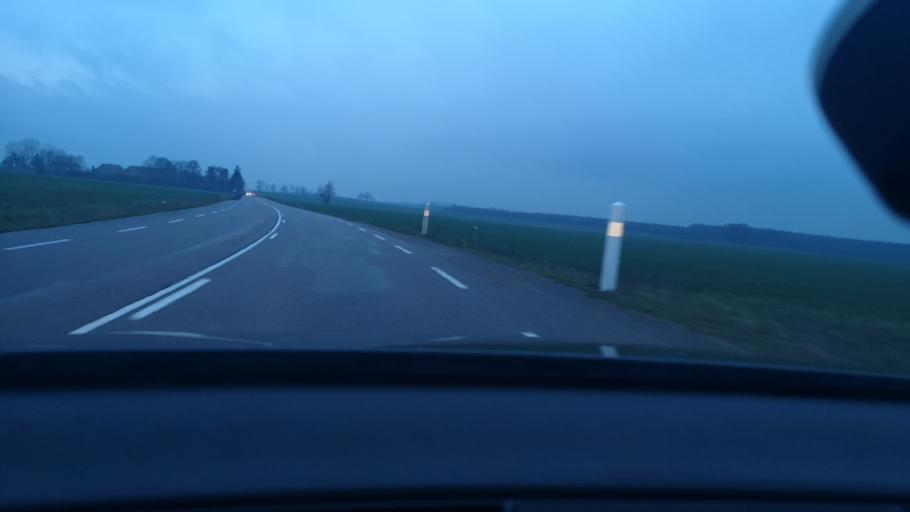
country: FR
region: Bourgogne
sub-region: Departement de Saone-et-Loire
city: Verdun-sur-le-Doubs
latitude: 47.0111
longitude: 4.9813
